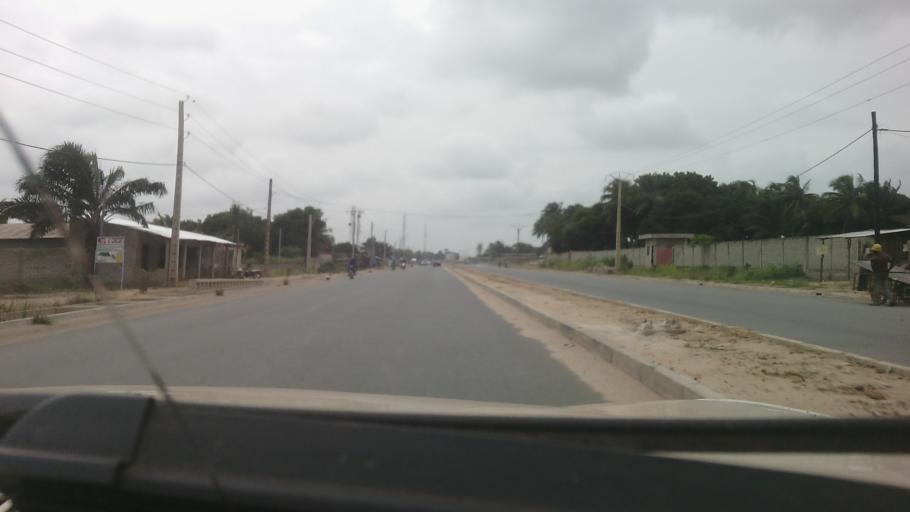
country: BJ
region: Atlantique
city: Hevie
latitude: 6.3847
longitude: 2.2009
